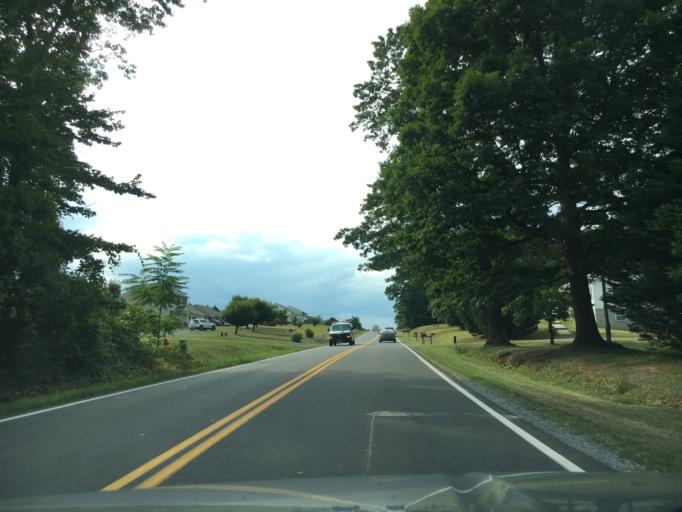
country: US
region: Virginia
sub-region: Campbell County
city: Rustburg
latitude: 37.2754
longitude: -79.1640
